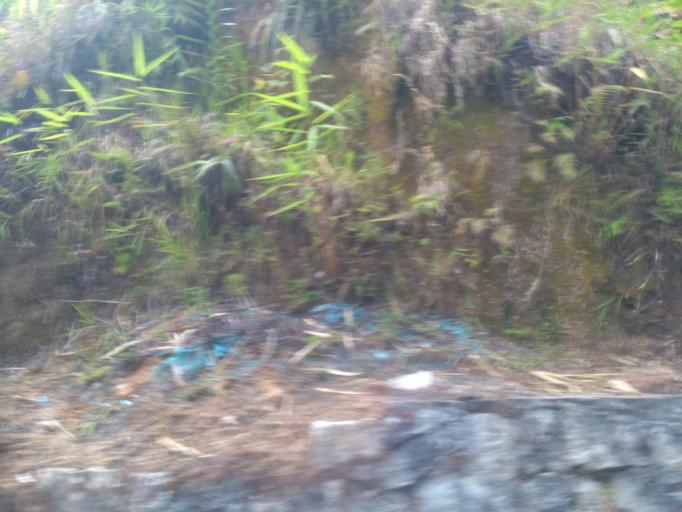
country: MY
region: Pahang
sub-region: Cameron Highlands
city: Tanah Rata
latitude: 4.4652
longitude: 101.3661
